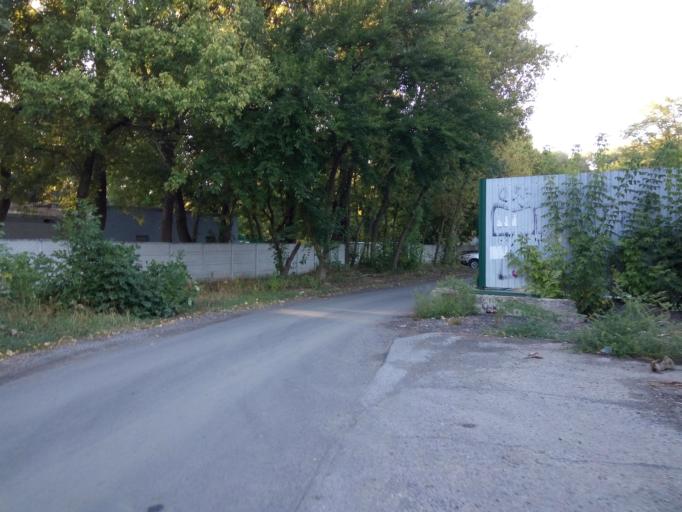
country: RU
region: Rostov
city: Rostov-na-Donu
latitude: 47.2446
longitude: 39.7577
